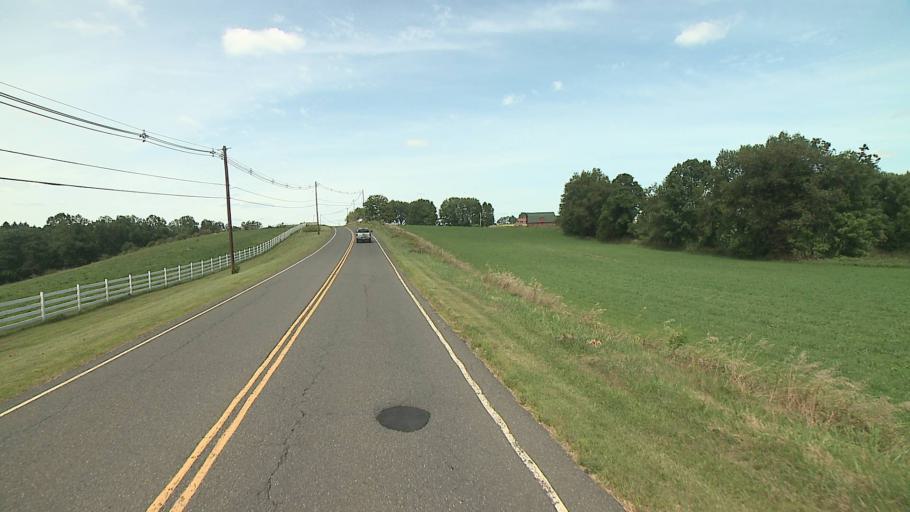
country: US
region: Connecticut
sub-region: Litchfield County
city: Bethlehem Village
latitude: 41.6094
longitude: -73.2439
